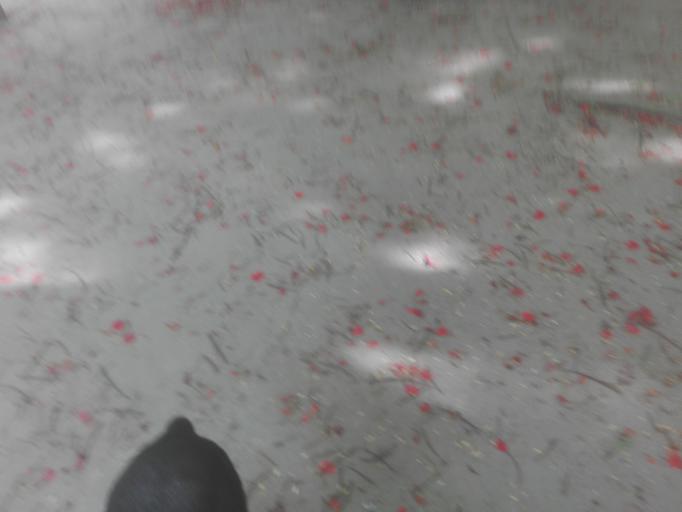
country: CO
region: Bolivar
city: Turbana
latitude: 10.1725
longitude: -75.7464
